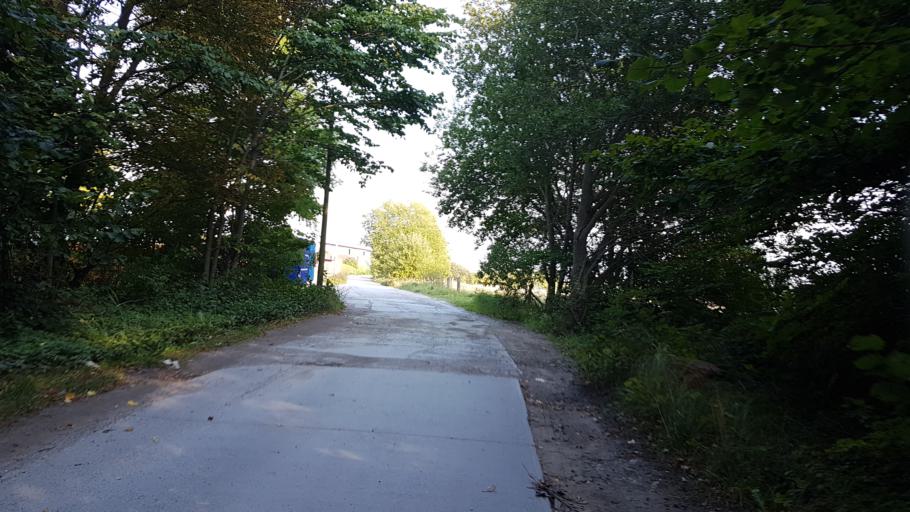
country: DE
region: Mecklenburg-Vorpommern
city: Sagard
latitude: 54.5020
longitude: 13.5345
